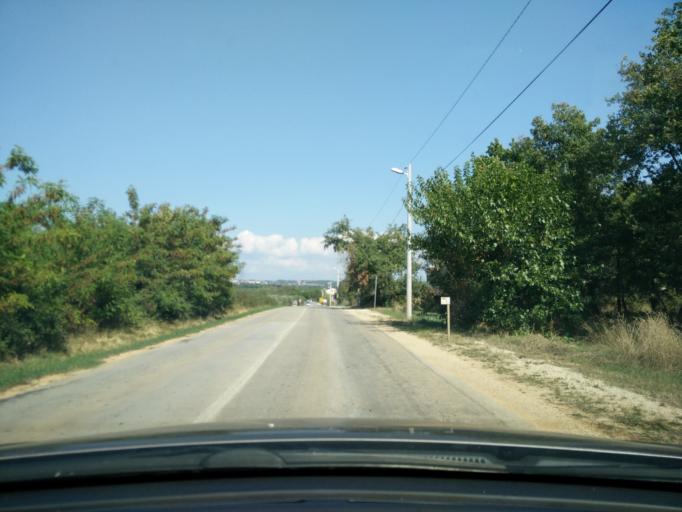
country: HR
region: Istarska
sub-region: Grad Porec
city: Porec
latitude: 45.2719
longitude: 13.6495
